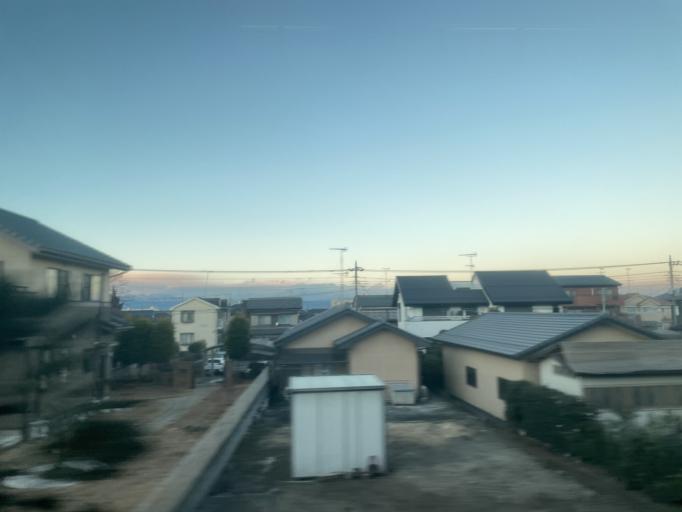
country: JP
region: Saitama
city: Fukayacho
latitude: 36.1945
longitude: 139.2685
